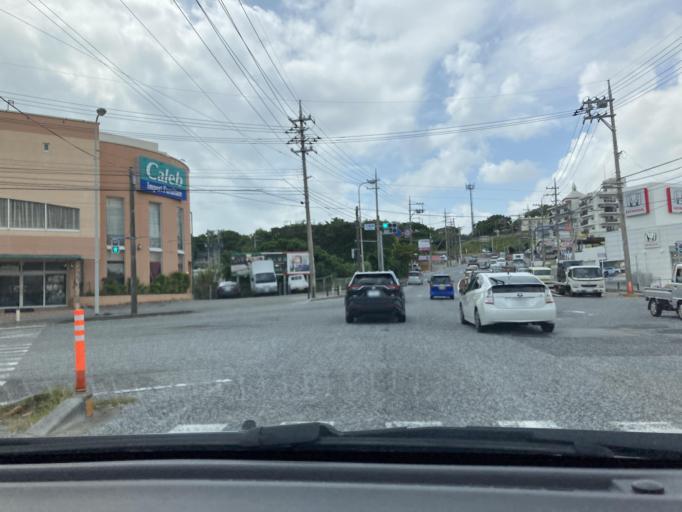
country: JP
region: Okinawa
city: Okinawa
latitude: 26.3185
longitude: 127.8206
